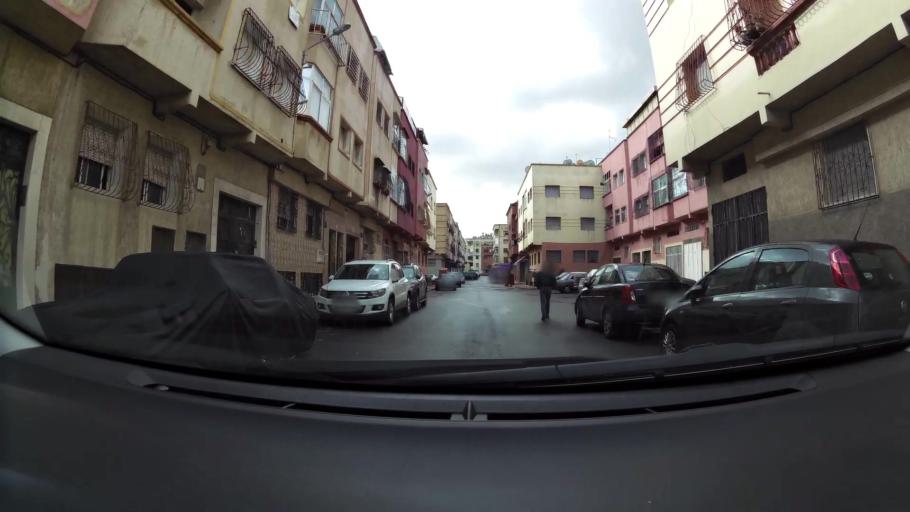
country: MA
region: Grand Casablanca
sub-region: Mediouna
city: Tit Mellil
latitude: 33.6019
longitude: -7.5357
